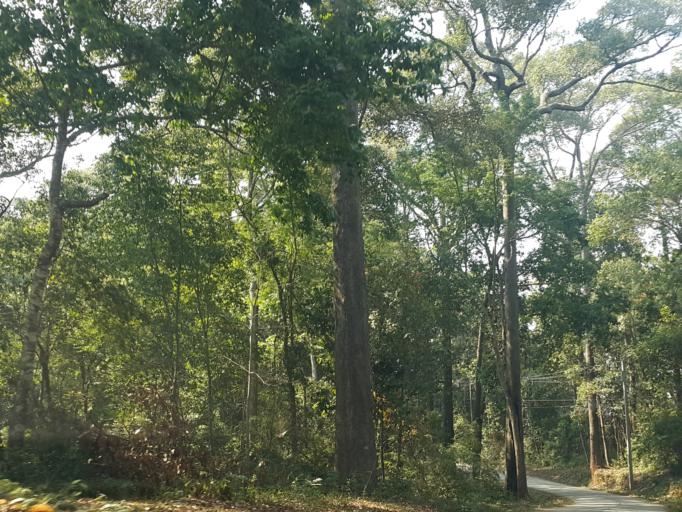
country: TH
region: Chiang Mai
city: Mae Taeng
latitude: 19.0229
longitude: 98.7938
